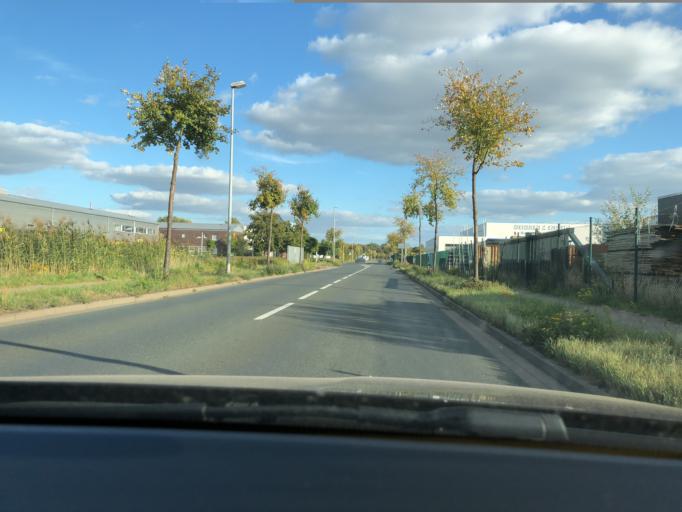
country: DE
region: Lower Saxony
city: Stuhr
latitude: 53.0228
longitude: 8.7680
